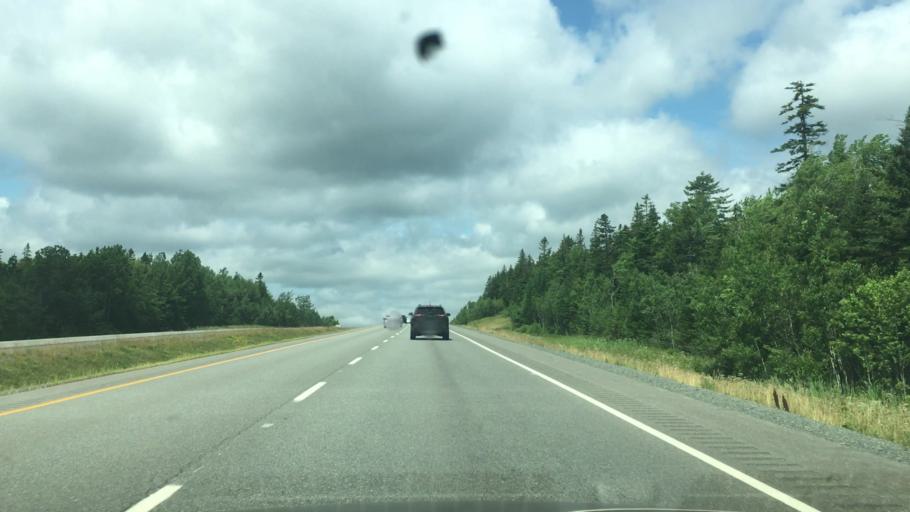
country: CA
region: Nova Scotia
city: Springhill
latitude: 45.7048
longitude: -64.0310
